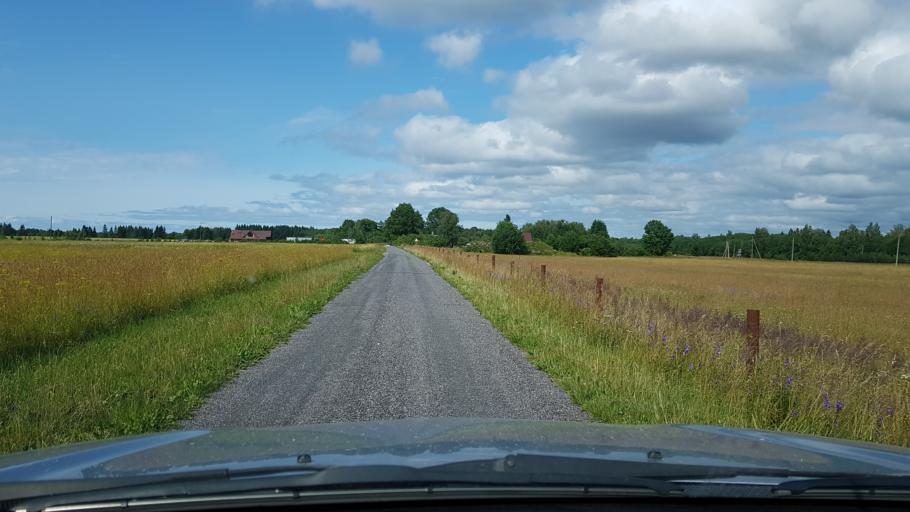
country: EE
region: Ida-Virumaa
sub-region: Narva-Joesuu linn
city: Narva-Joesuu
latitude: 59.3690
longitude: 27.9536
